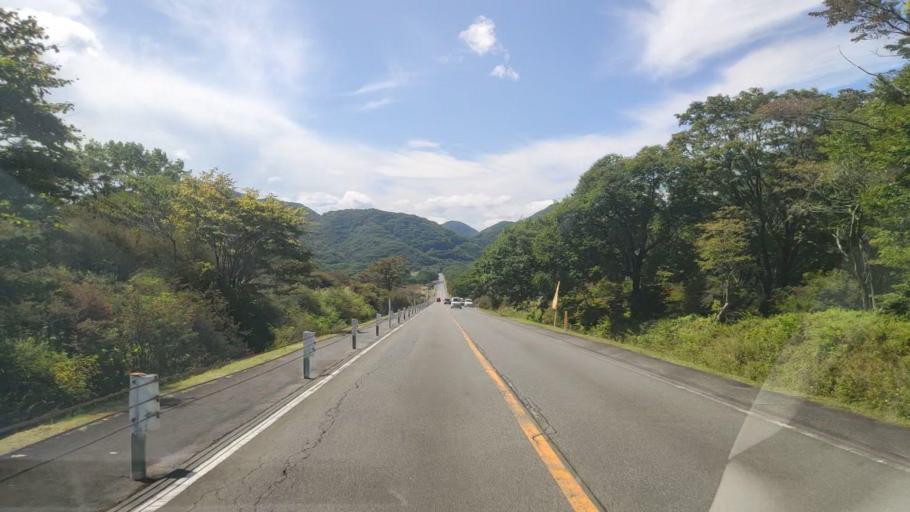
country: JP
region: Gunma
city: Shibukawa
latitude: 36.4782
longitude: 138.8920
